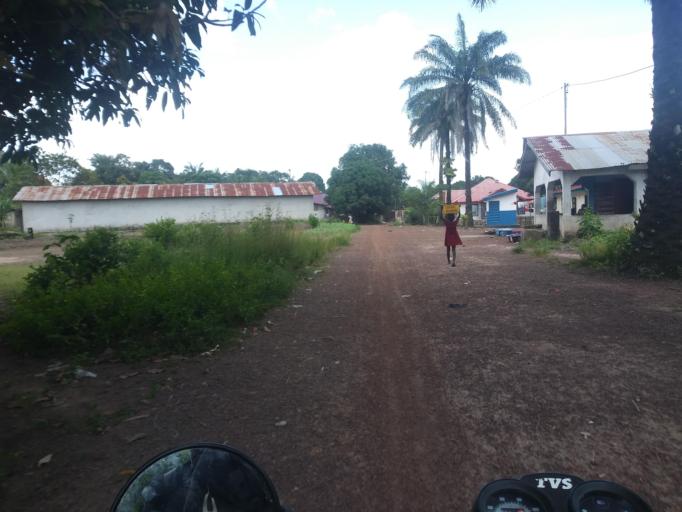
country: SL
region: Northern Province
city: Makeni
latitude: 8.8716
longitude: -12.0417
